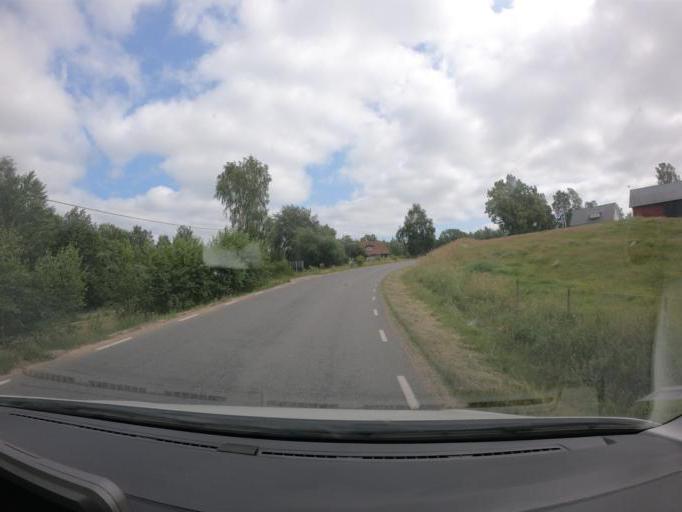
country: SE
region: Skane
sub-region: Hassleholms Kommun
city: Tormestorp
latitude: 56.1421
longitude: 13.6287
